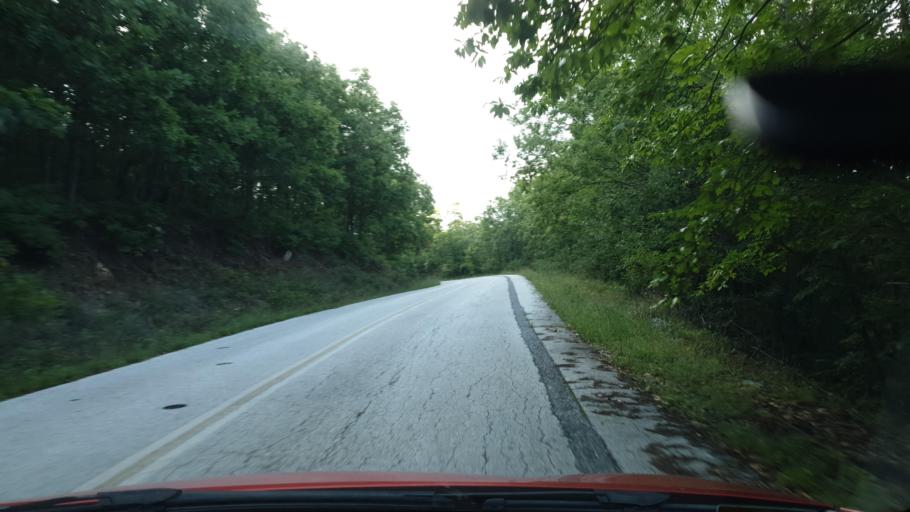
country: GR
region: Central Macedonia
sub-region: Nomos Chalkidikis
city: Galatista
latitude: 40.5121
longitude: 23.2684
